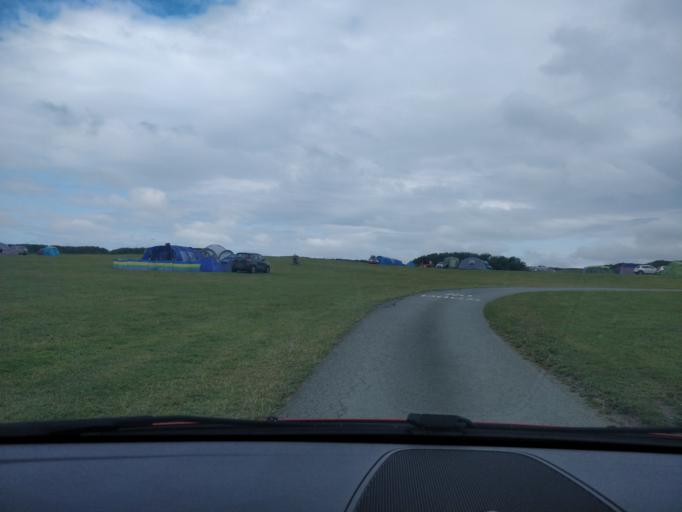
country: GB
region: Wales
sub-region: Gwynedd
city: Llanfair
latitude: 52.8159
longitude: -4.1455
